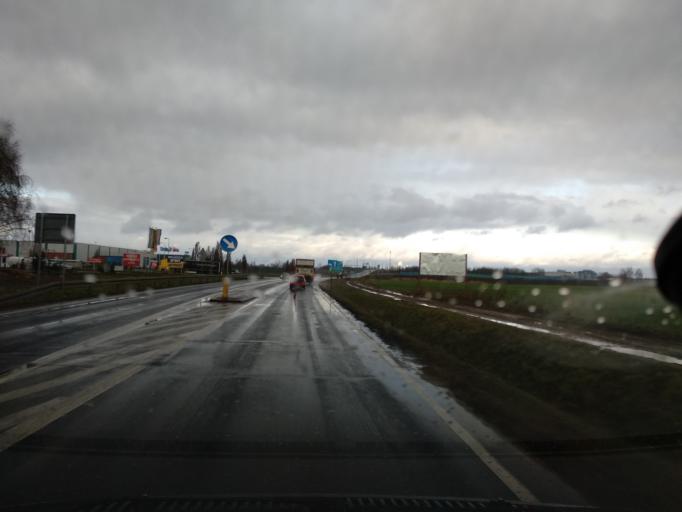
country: PL
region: Greater Poland Voivodeship
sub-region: Powiat koninski
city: Stare Miasto
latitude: 52.1574
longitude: 18.2055
